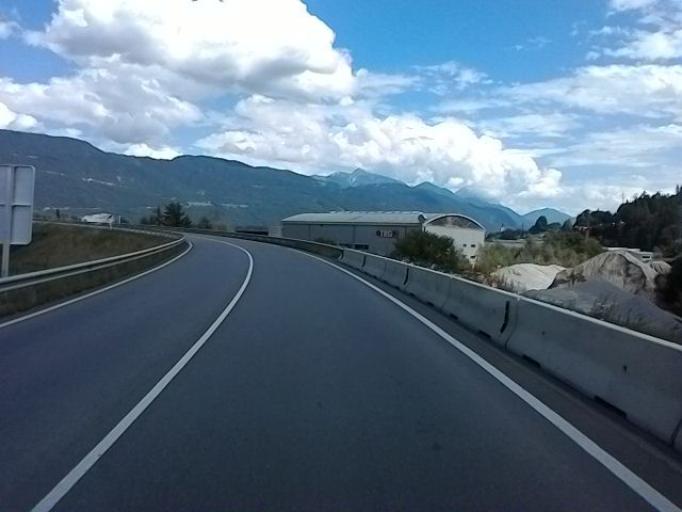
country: AT
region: Tyrol
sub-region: Politischer Bezirk Innsbruck Land
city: Telfs
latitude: 47.2987
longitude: 11.0685
